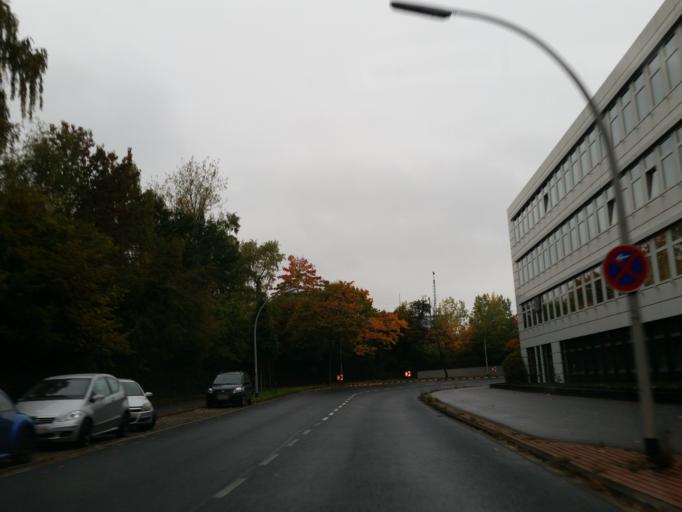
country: DE
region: Lower Saxony
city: Braunschweig
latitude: 52.2508
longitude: 10.5430
